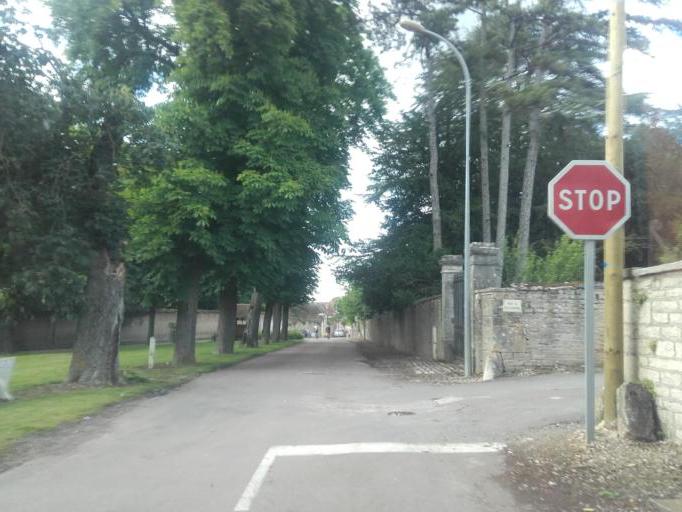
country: FR
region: Bourgogne
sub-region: Departement de Saone-et-Loire
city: Rully
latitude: 46.8718
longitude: 4.7428
